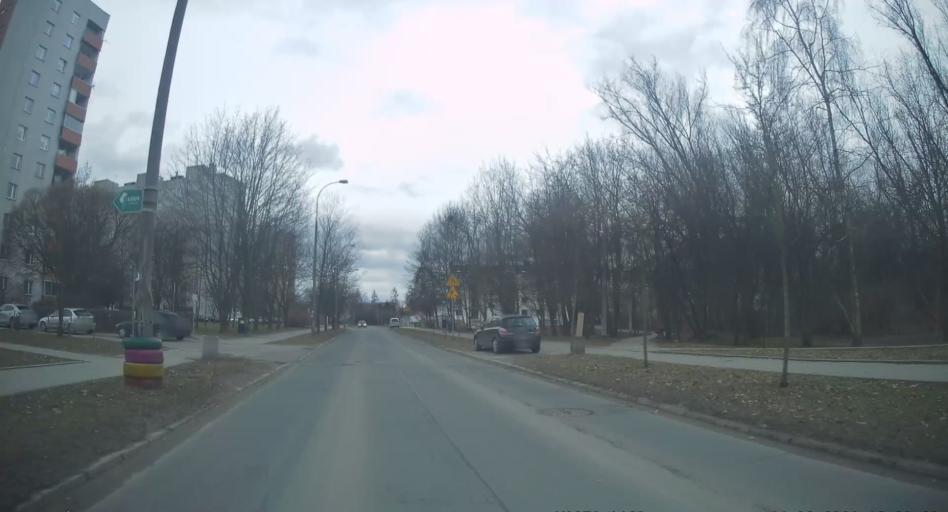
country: PL
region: Lesser Poland Voivodeship
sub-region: Powiat wielicki
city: Czarnochowice
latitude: 50.0111
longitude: 20.0167
